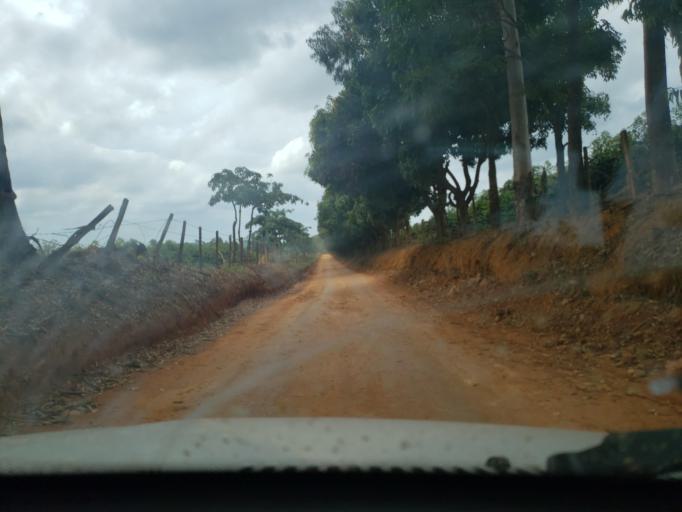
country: BR
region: Minas Gerais
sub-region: Boa Esperanca
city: Boa Esperanca
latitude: -20.9878
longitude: -45.5951
